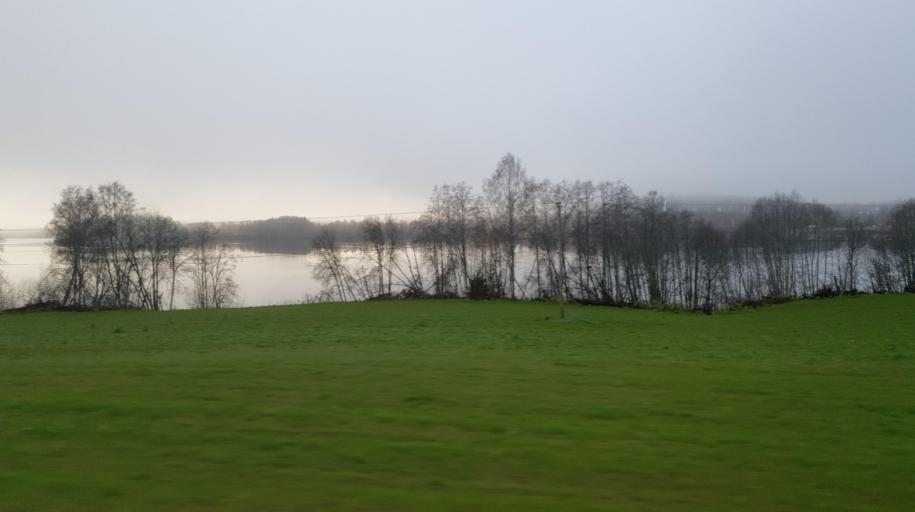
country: NO
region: Buskerud
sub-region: Krodsherad
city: Noresund
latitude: 60.1488
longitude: 9.7611
